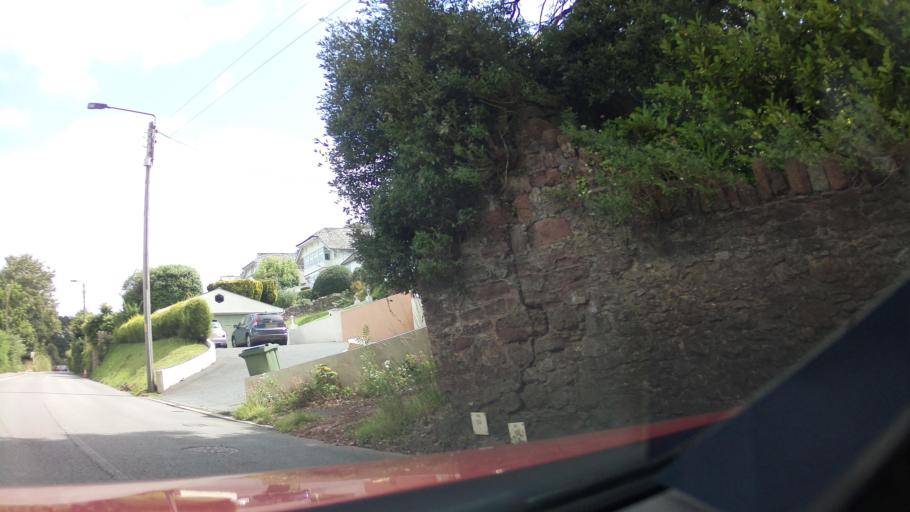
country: GB
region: England
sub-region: Devon
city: Teignmouth
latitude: 50.5389
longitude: -3.5084
